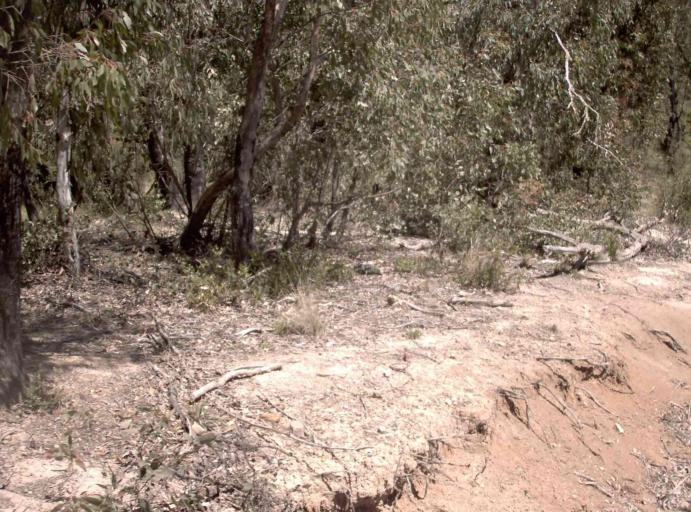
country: AU
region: Victoria
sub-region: East Gippsland
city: Lakes Entrance
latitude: -37.1281
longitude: 148.2450
